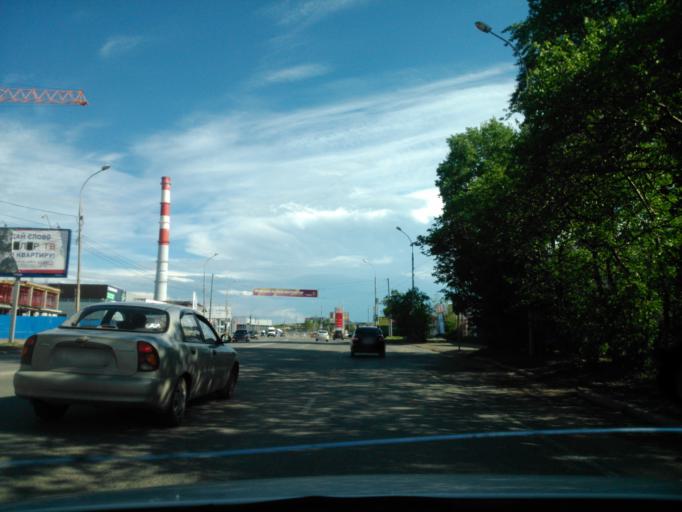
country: RU
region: Perm
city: Froly
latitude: 57.9627
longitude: 56.2632
